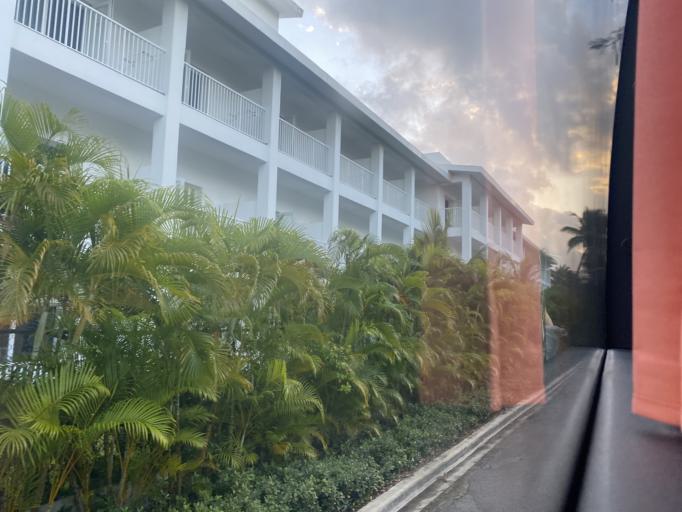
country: DO
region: San Juan
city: Punta Cana
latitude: 18.7199
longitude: -68.4574
